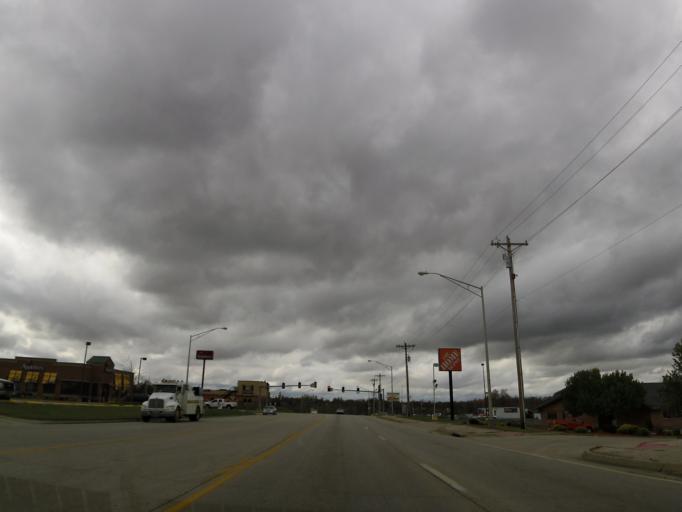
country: US
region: Missouri
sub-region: Butler County
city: Poplar Bluff
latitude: 36.7495
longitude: -90.4104
